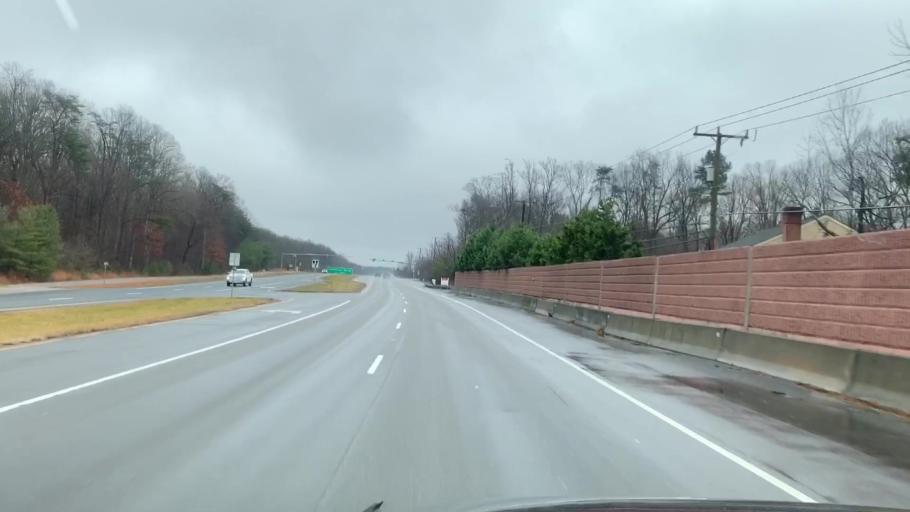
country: US
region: Virginia
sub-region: Fairfax County
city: Burke
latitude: 38.7548
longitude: -77.3041
